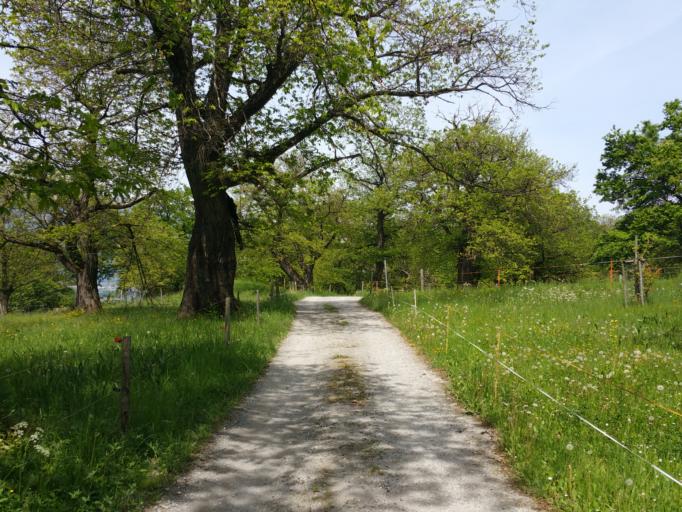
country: CH
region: Vaud
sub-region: Aigle District
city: Bex
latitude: 46.2564
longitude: 7.0097
